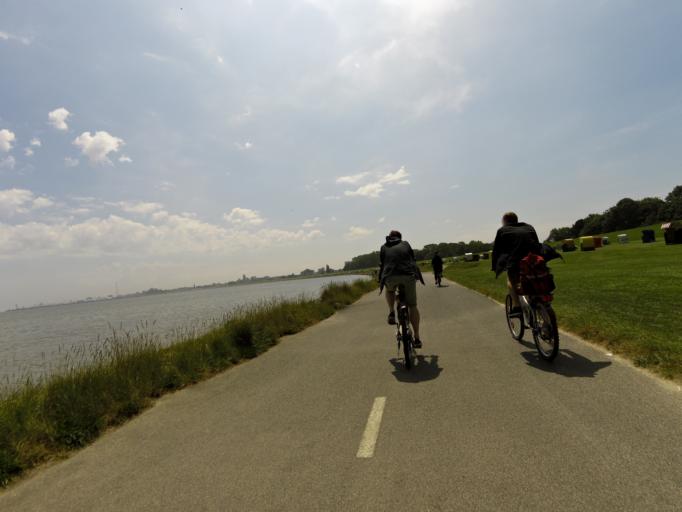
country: DE
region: Lower Saxony
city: Cuxhaven
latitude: 53.8886
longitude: 8.6833
